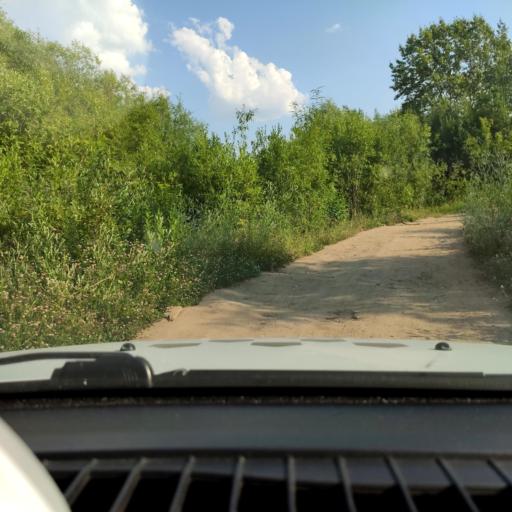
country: RU
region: Perm
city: Perm
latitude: 58.0238
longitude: 56.2115
